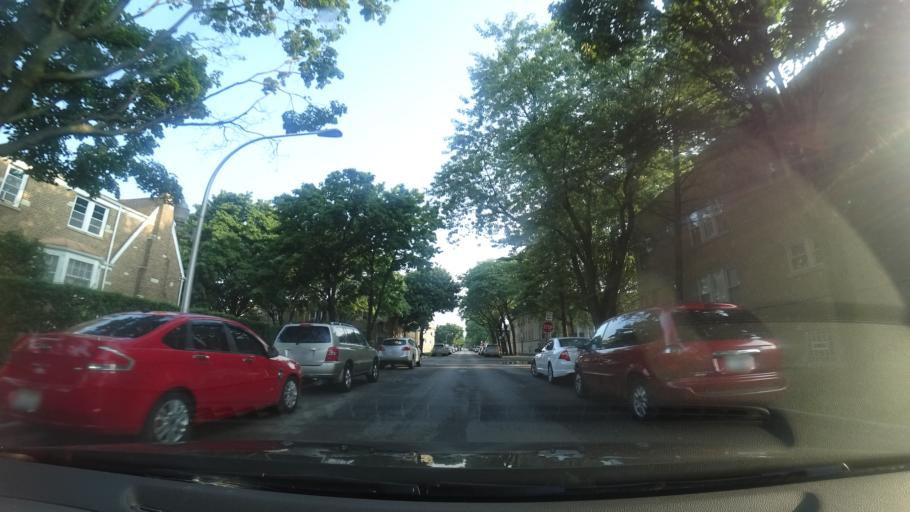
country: US
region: Illinois
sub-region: Cook County
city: Oak Park
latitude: 41.9283
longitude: -87.7539
